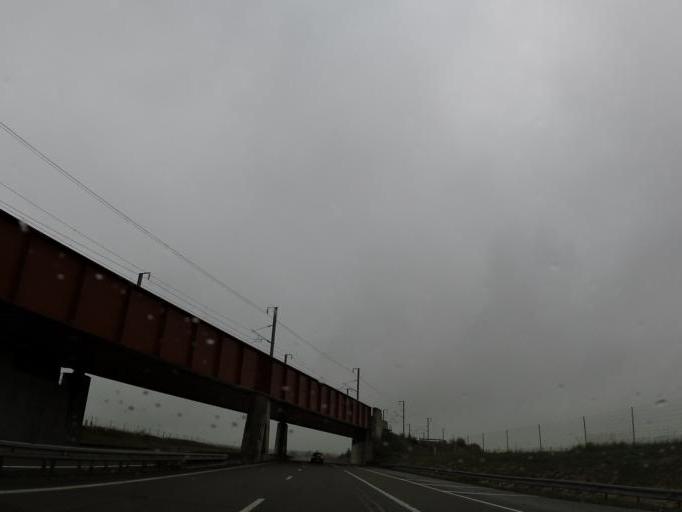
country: FR
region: Champagne-Ardenne
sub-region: Departement de la Marne
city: Courtisols
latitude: 49.0321
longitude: 4.5563
